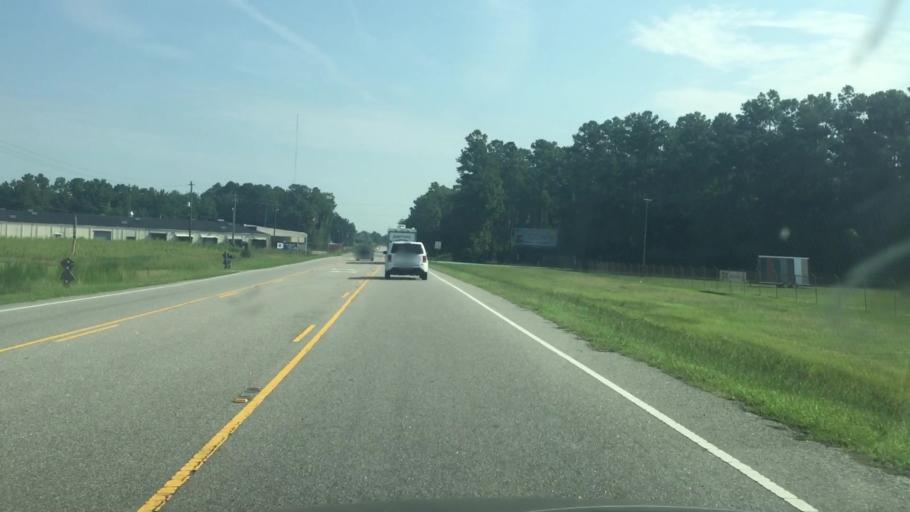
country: US
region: North Carolina
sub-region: Columbus County
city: Tabor City
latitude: 34.1449
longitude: -78.8640
